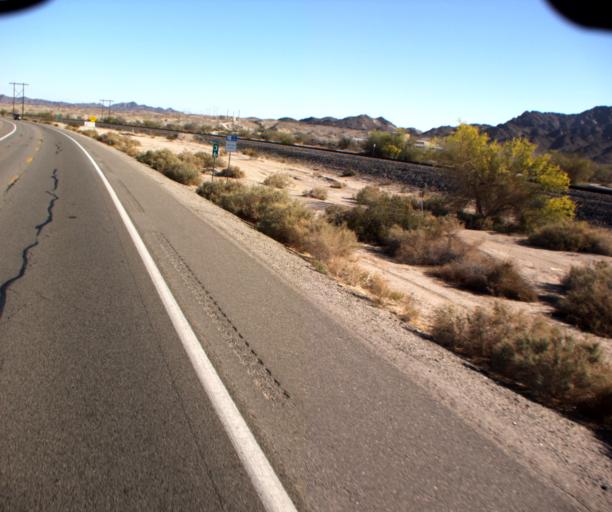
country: US
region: Arizona
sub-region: Yuma County
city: Fortuna Foothills
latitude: 32.7230
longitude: -114.4214
